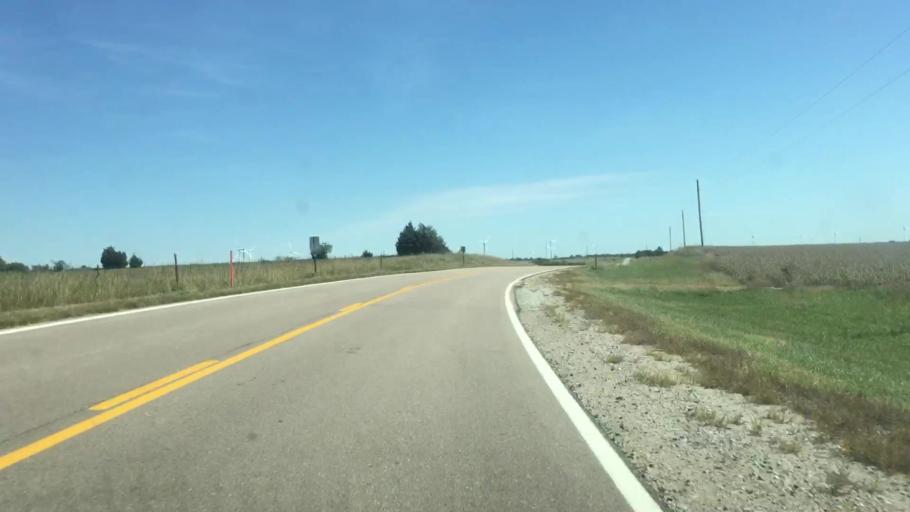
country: US
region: Nebraska
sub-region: Jefferson County
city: Fairbury
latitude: 40.0449
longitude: -97.0049
